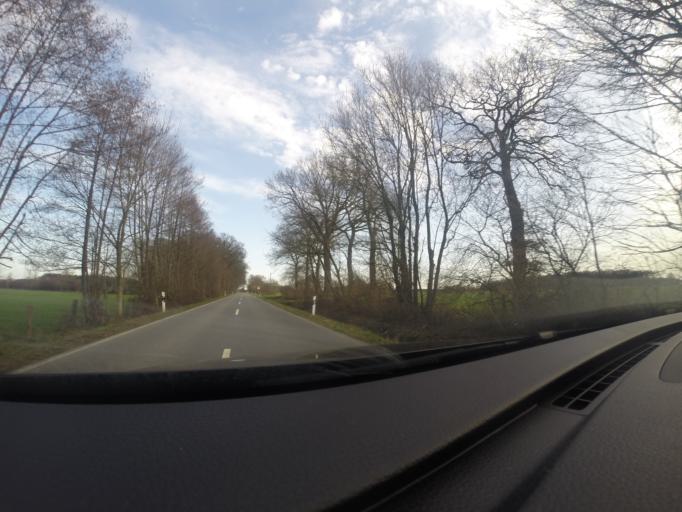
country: DE
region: North Rhine-Westphalia
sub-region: Regierungsbezirk Munster
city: Schoppingen
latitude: 52.0517
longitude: 7.1944
